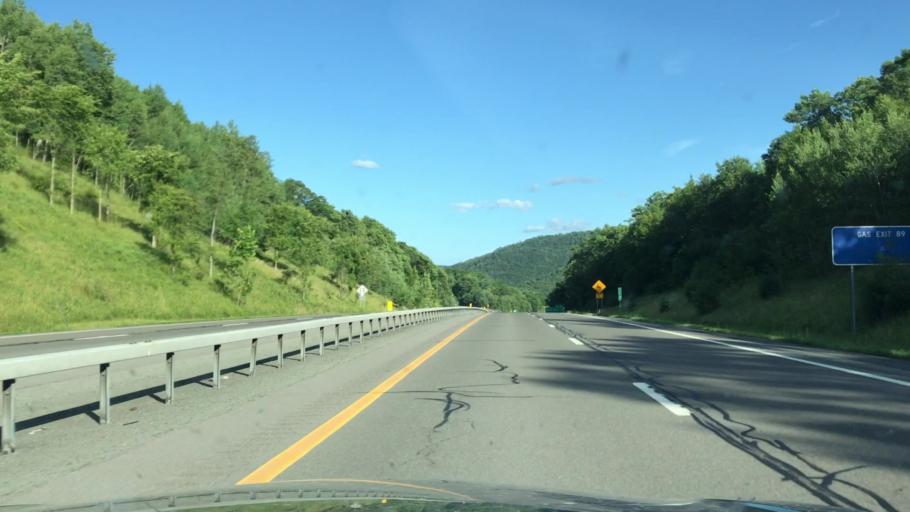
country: US
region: New York
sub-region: Delaware County
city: Hancock
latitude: 41.9733
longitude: -75.1927
